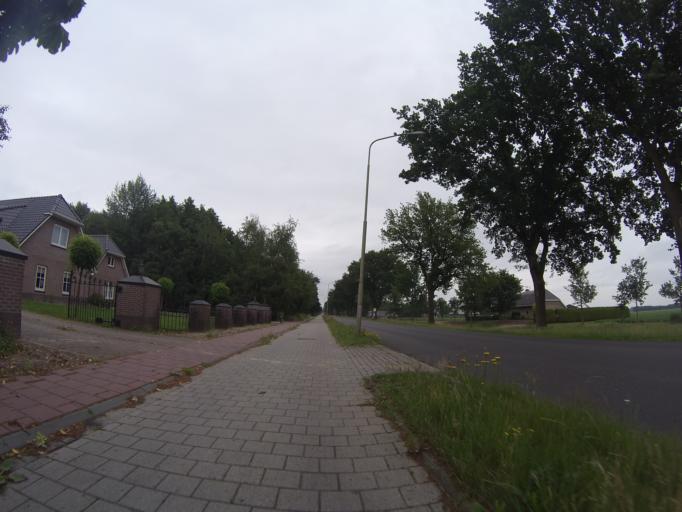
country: NL
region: Drenthe
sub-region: Gemeente Emmen
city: Emmen
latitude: 52.8035
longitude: 6.9721
